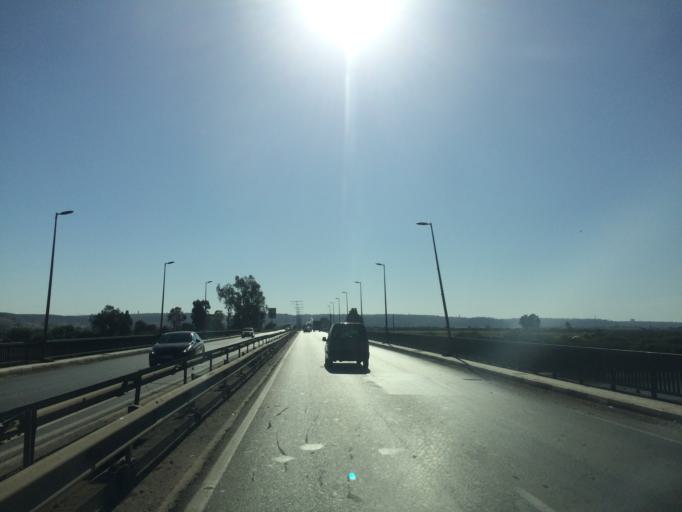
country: MA
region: Rabat-Sale-Zemmour-Zaer
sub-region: Rabat
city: Rabat
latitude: 33.9890
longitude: -6.7661
